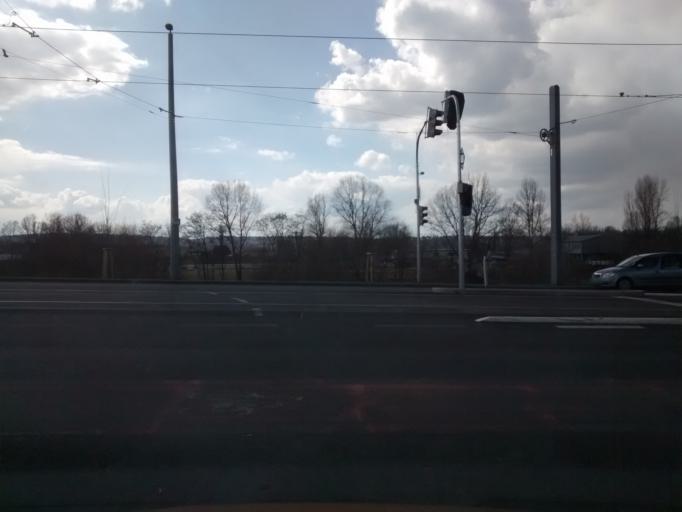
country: CZ
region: Praha
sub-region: Praha 8
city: Karlin
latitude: 50.1148
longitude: 14.4353
